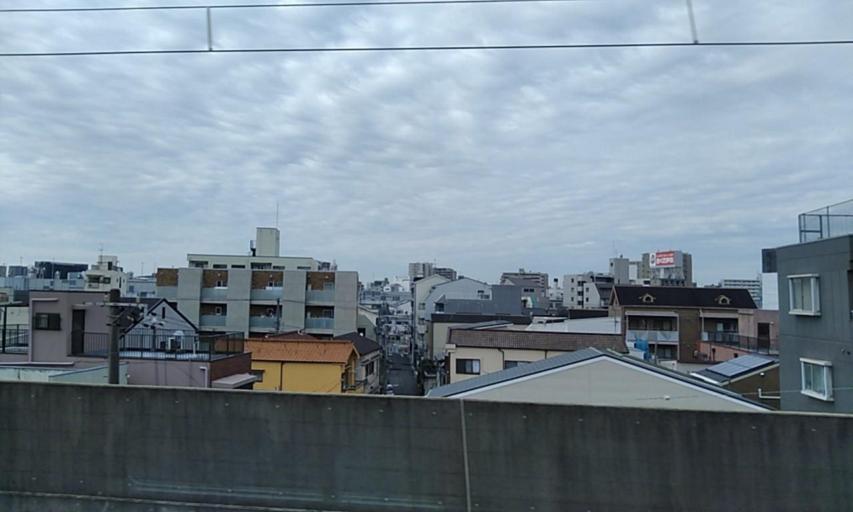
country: JP
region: Osaka
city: Matsubara
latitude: 34.6253
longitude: 135.5314
